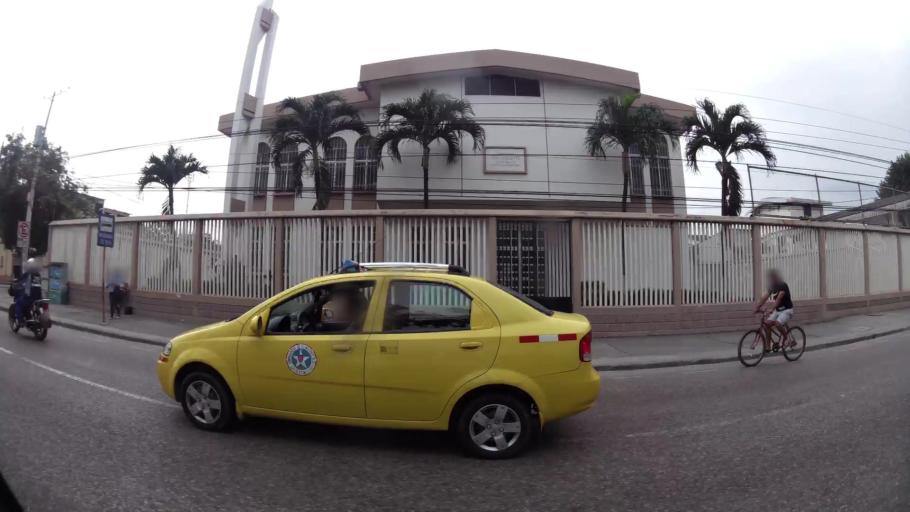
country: EC
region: Guayas
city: Eloy Alfaro
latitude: -2.1709
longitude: -79.8856
